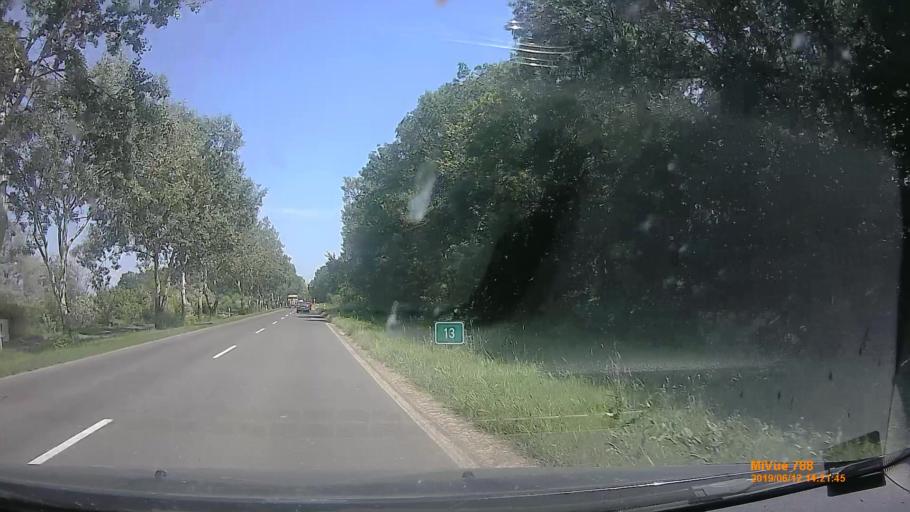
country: HU
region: Csongrad
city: Deszk
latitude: 46.2186
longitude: 20.2640
